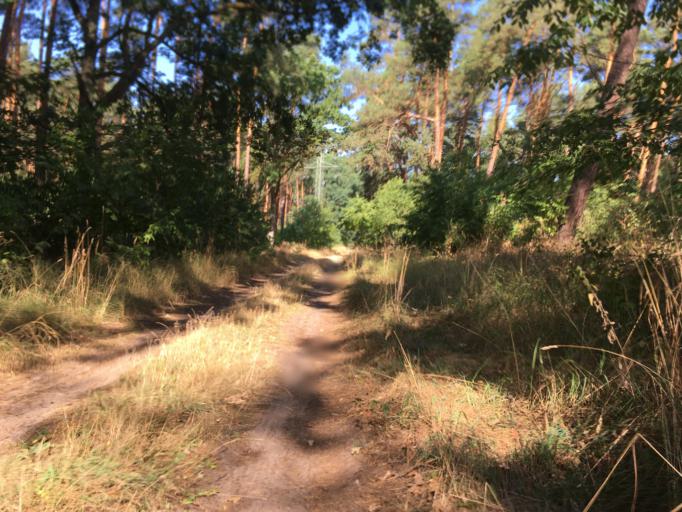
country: DE
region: Brandenburg
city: Zehdenick
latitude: 52.9487
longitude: 13.3909
